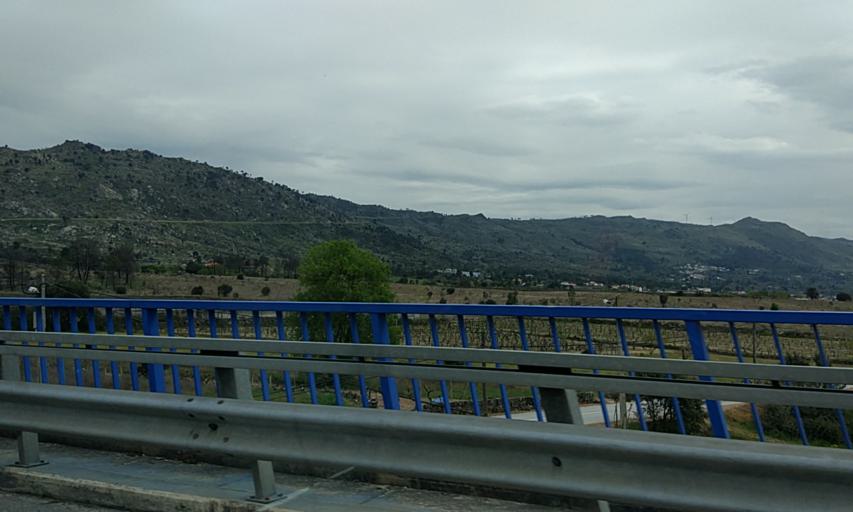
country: PT
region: Guarda
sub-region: Guarda
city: Guarda
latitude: 40.6220
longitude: -7.2978
